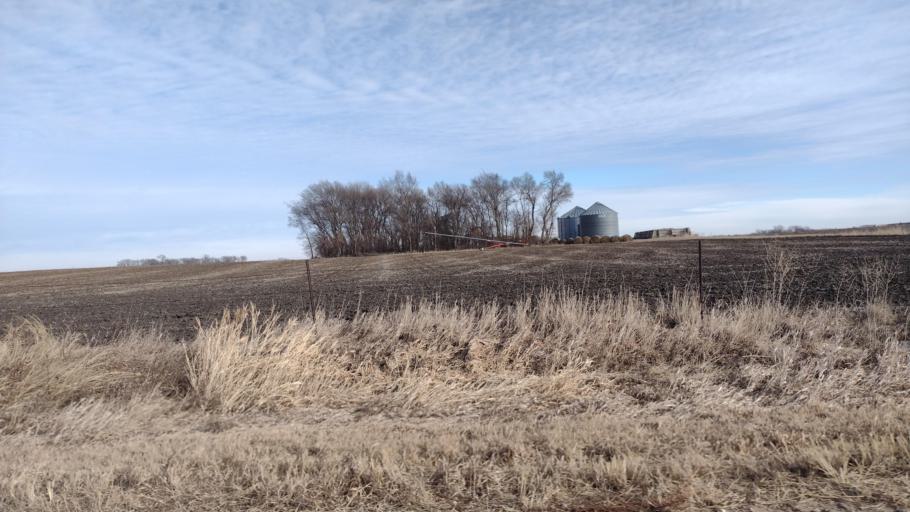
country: US
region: South Dakota
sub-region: Union County
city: Beresford
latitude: 42.9587
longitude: -96.8054
